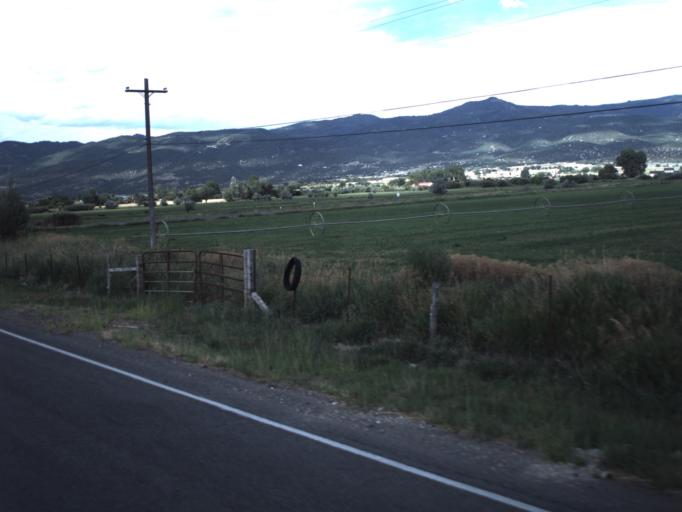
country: US
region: Utah
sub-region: Sanpete County
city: Mount Pleasant
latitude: 39.5816
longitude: -111.4549
